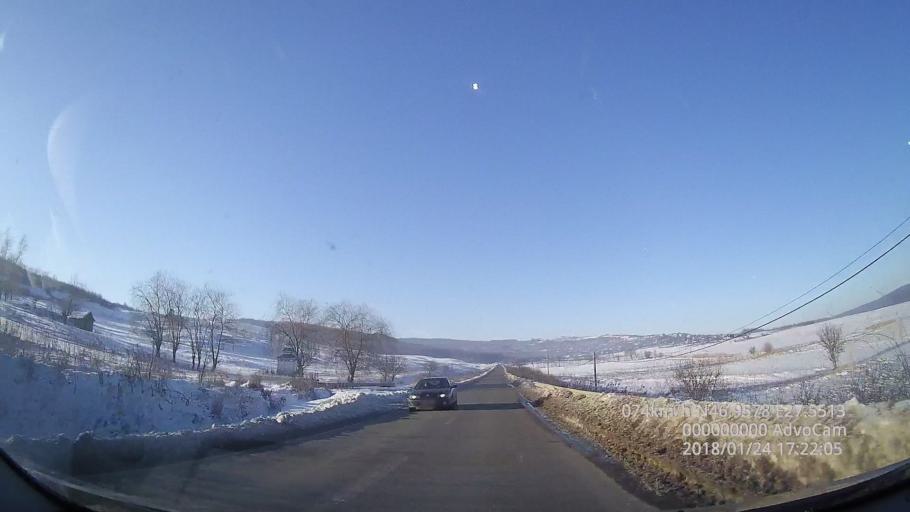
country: RO
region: Iasi
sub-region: Comuna Grajduri
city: Grajduri
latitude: 46.9581
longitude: 27.5508
